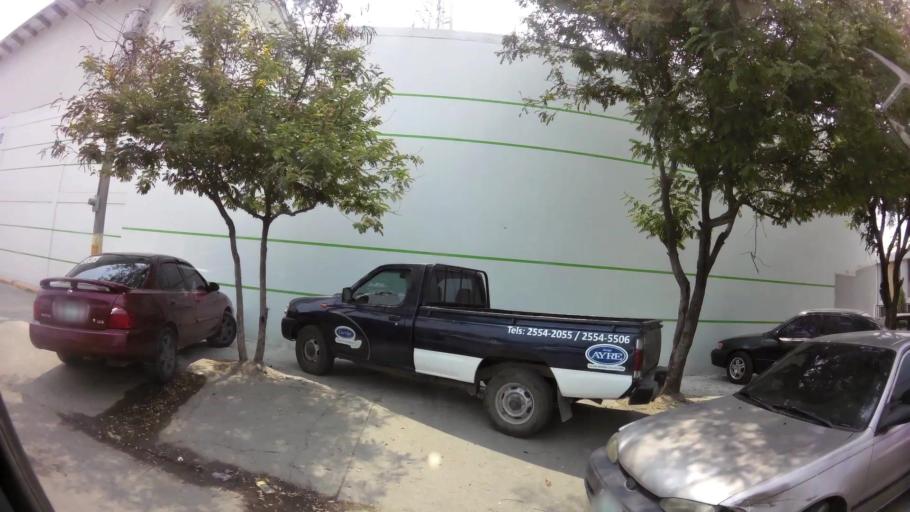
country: HN
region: Cortes
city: San Pedro Sula
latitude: 15.4818
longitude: -88.0212
